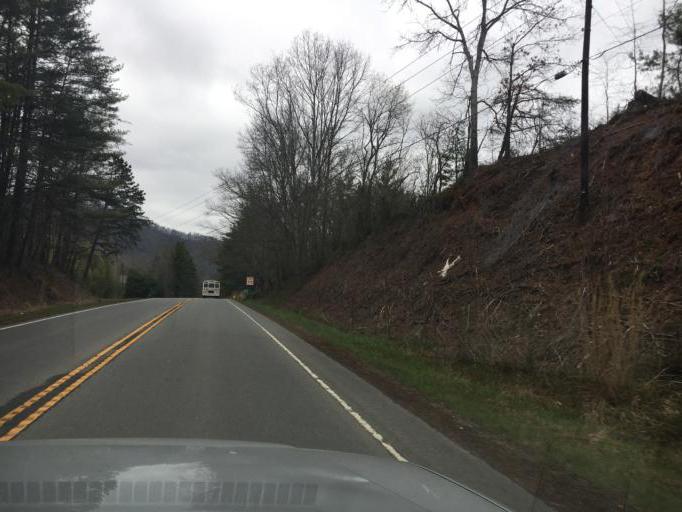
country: US
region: North Carolina
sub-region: Madison County
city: Mars Hill
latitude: 35.7756
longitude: -82.5031
